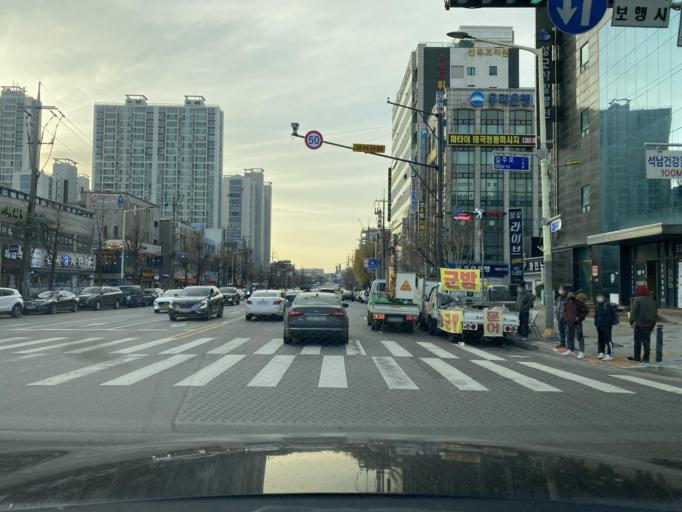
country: KR
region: Incheon
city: Incheon
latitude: 37.5064
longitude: 126.6723
